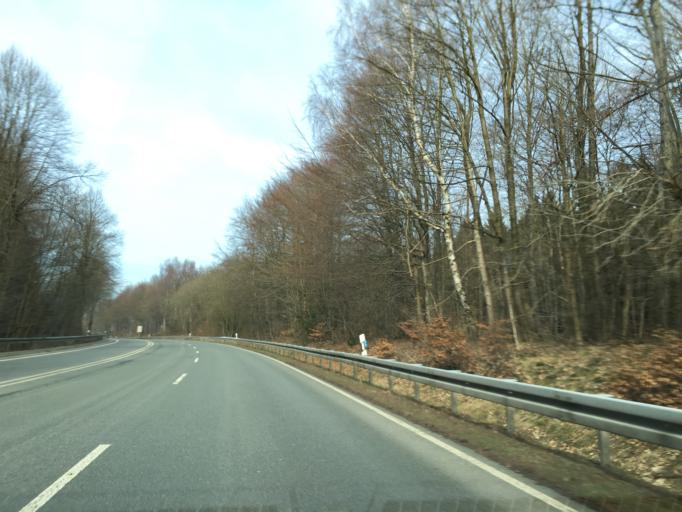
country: DE
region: North Rhine-Westphalia
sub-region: Regierungsbezirk Detmold
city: Willebadessen
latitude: 51.5698
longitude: 9.0037
